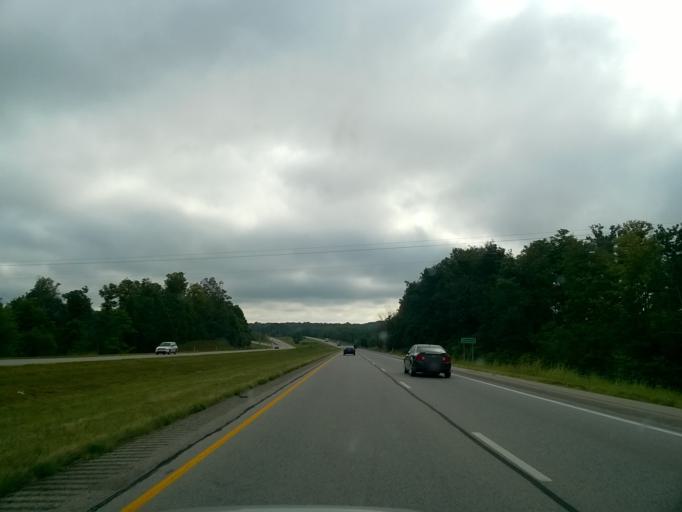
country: US
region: Indiana
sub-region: Floyd County
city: Georgetown
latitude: 38.2716
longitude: -85.9726
